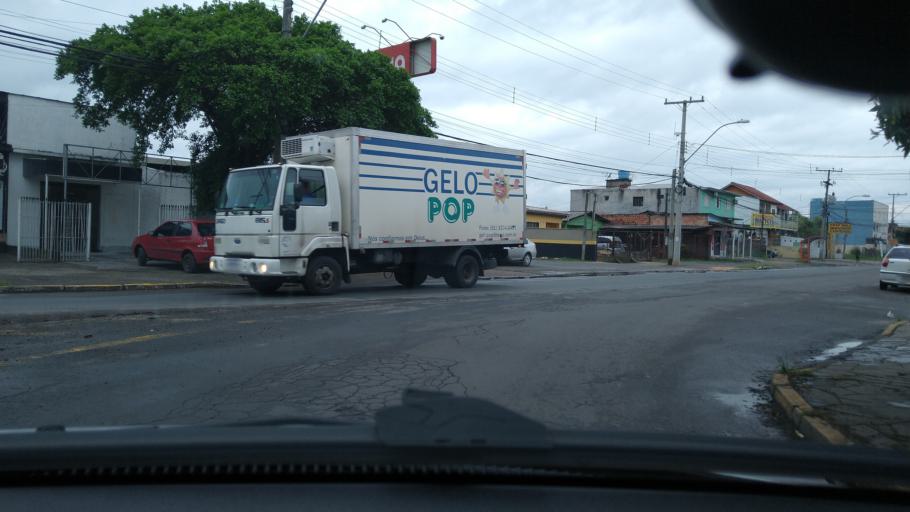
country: BR
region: Rio Grande do Sul
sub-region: Canoas
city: Canoas
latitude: -29.9022
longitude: -51.2032
